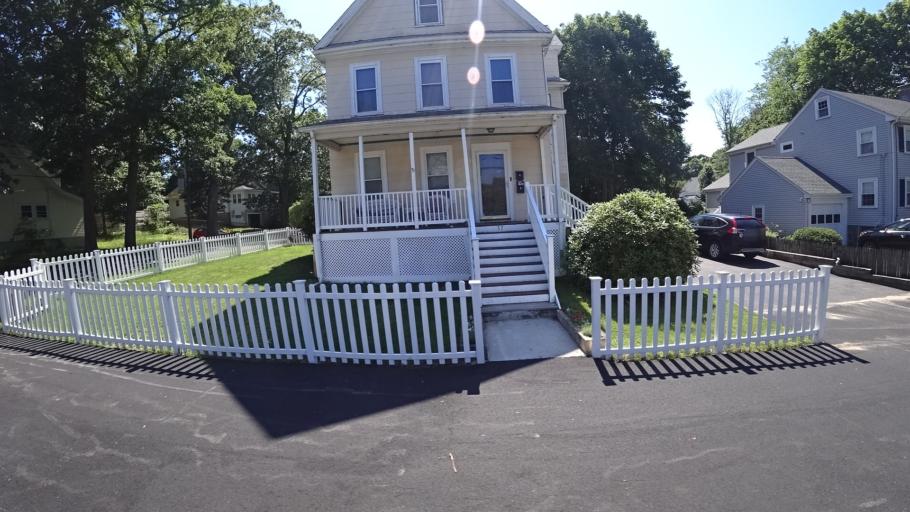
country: US
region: Massachusetts
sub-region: Norfolk County
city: Dedham
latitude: 42.2397
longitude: -71.1505
